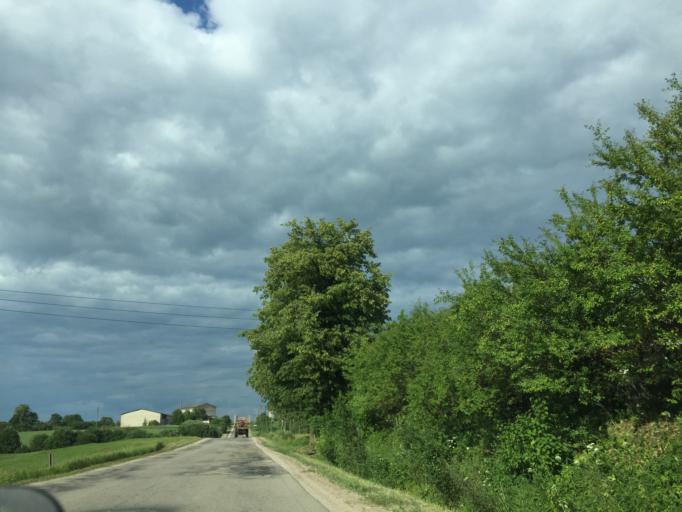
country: LV
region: Skriveri
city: Skriveri
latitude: 56.8394
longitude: 25.1418
